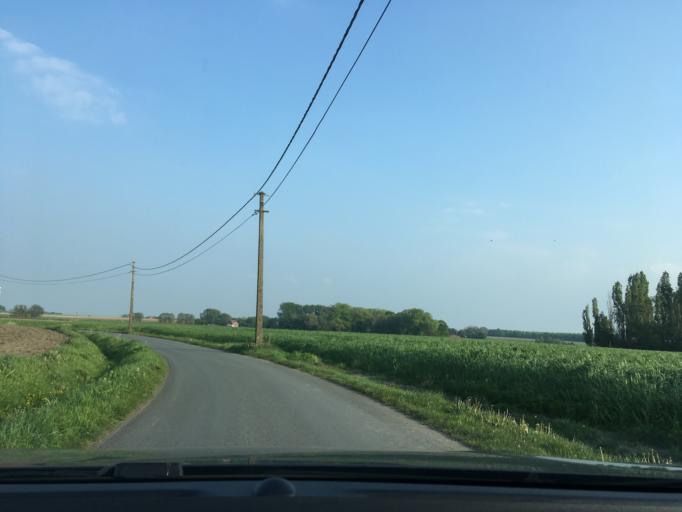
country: BE
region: Flanders
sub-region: Provincie West-Vlaanderen
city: Lichtervelde
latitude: 51.0140
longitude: 3.1466
